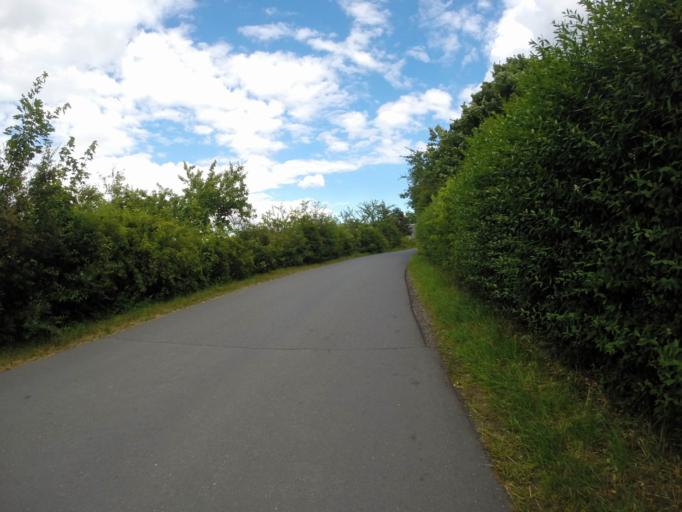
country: DE
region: Thuringia
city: Grosslobichau
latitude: 50.9306
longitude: 11.6497
